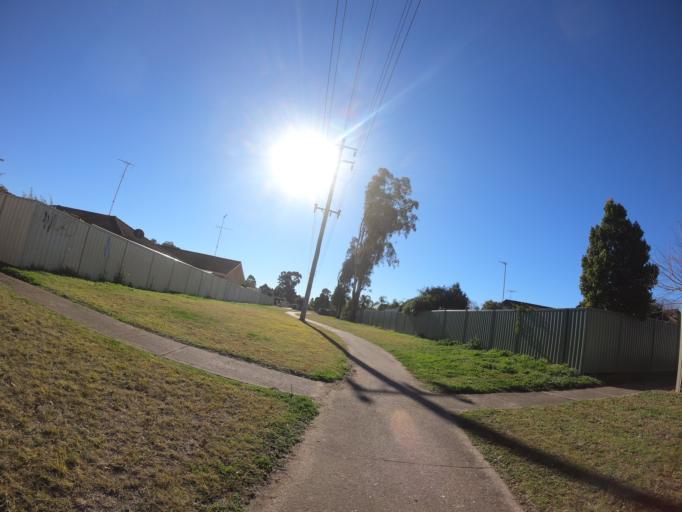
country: AU
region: New South Wales
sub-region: Hawkesbury
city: South Windsor
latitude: -33.6357
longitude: 150.7919
